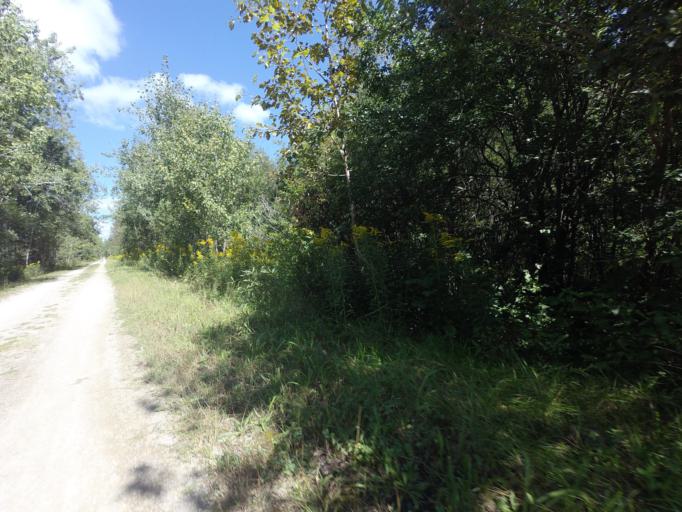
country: CA
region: Ontario
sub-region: Wellington County
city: Guelph
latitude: 43.7538
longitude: -80.3208
